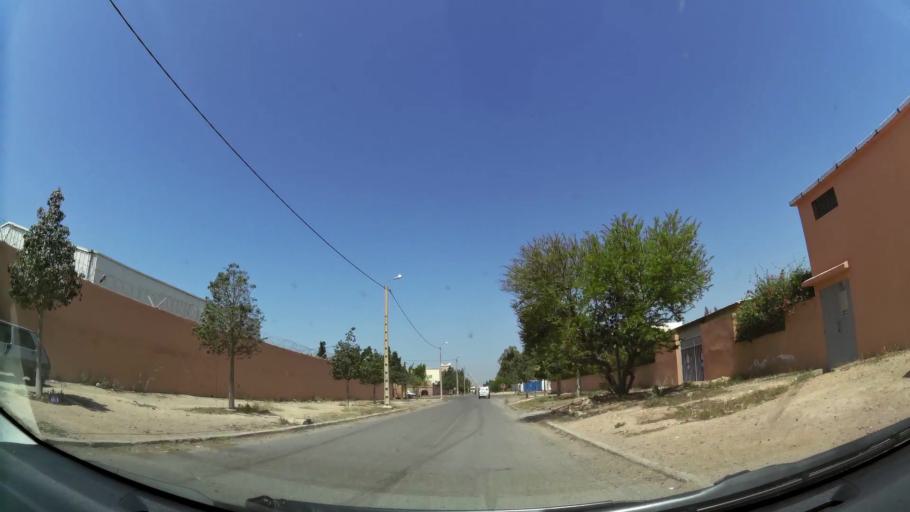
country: MA
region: Souss-Massa-Draa
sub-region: Inezgane-Ait Mellou
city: Inezgane
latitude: 30.3346
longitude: -9.4861
